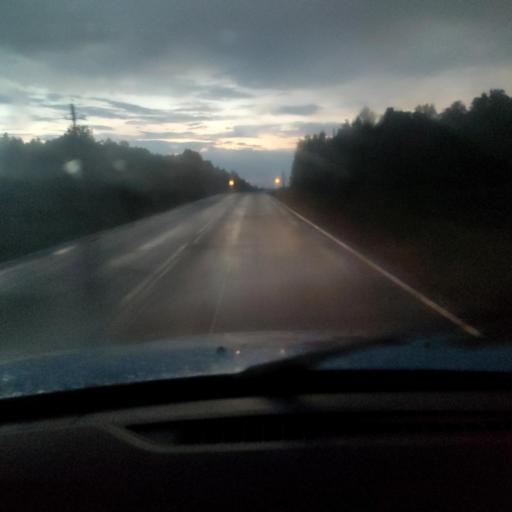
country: RU
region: Bashkortostan
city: Ulukulevo
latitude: 54.5346
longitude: 56.3682
